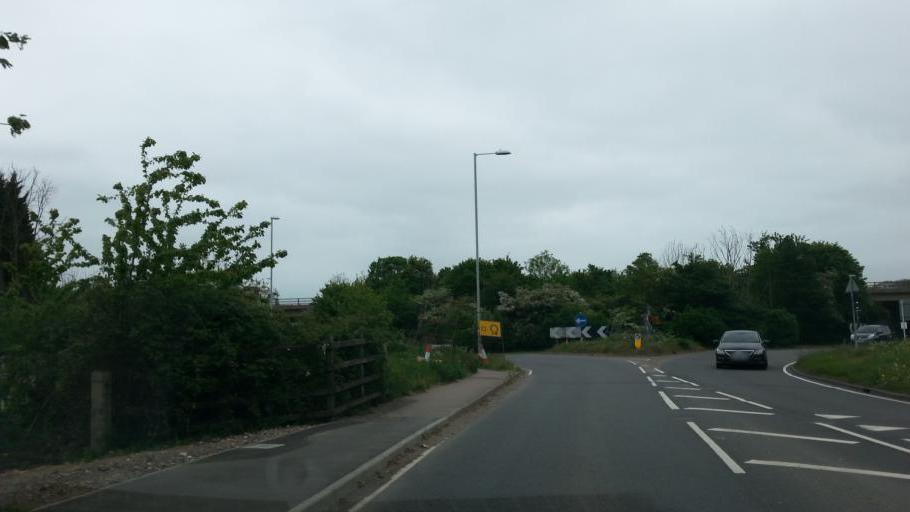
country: GB
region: England
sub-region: Cambridgeshire
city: Godmanchester
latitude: 52.3177
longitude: -0.1600
